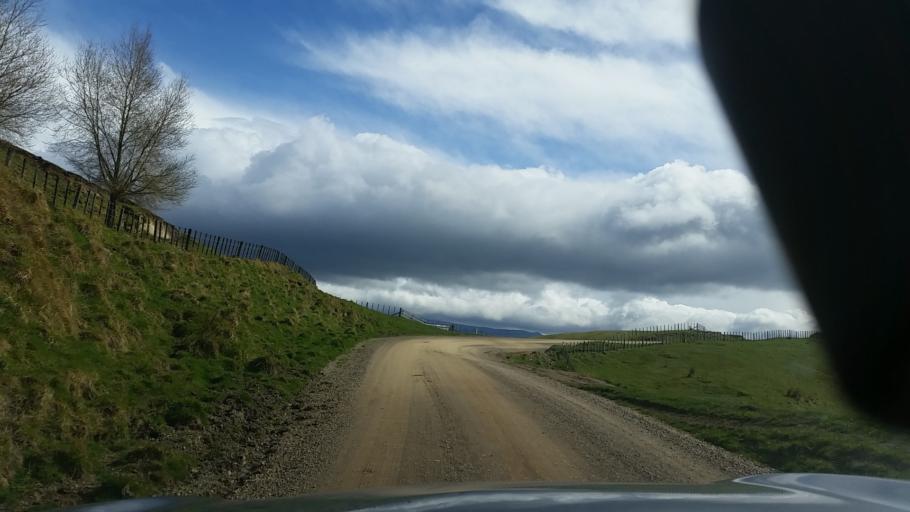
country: NZ
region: Hawke's Bay
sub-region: Napier City
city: Napier
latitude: -39.2036
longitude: 176.9526
